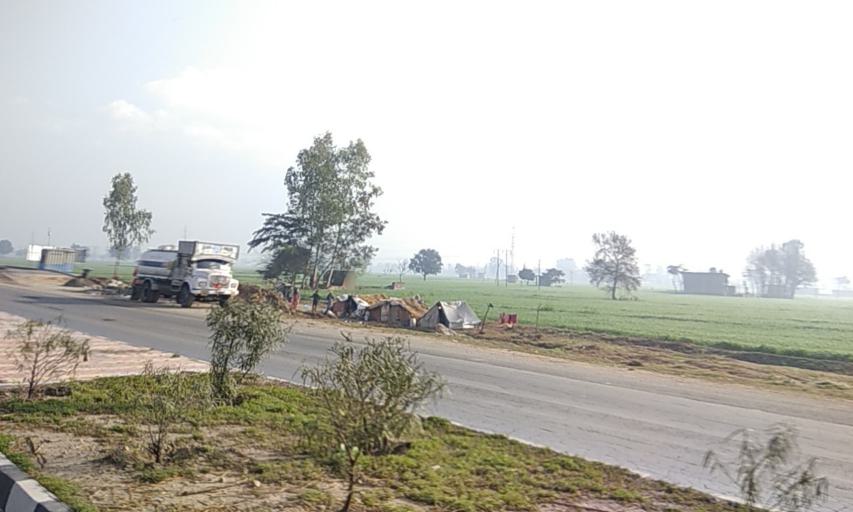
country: IN
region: Punjab
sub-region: Gurdaspur
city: Dinanagar
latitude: 32.1951
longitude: 75.5322
